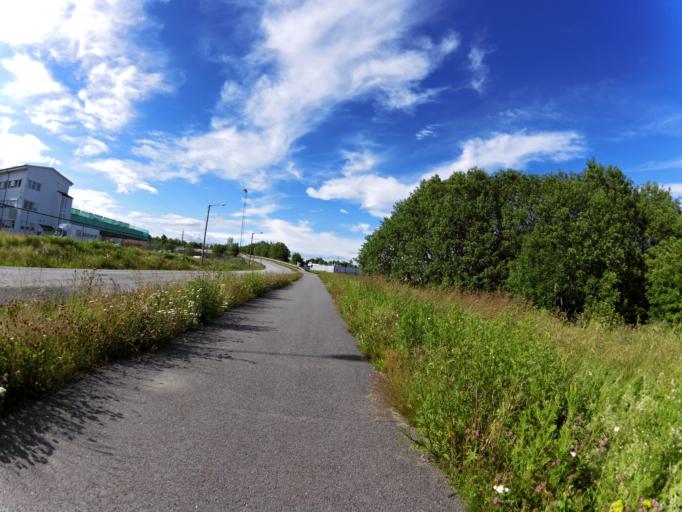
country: NO
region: Ostfold
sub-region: Fredrikstad
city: Fredrikstad
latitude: 59.2569
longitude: 11.0112
